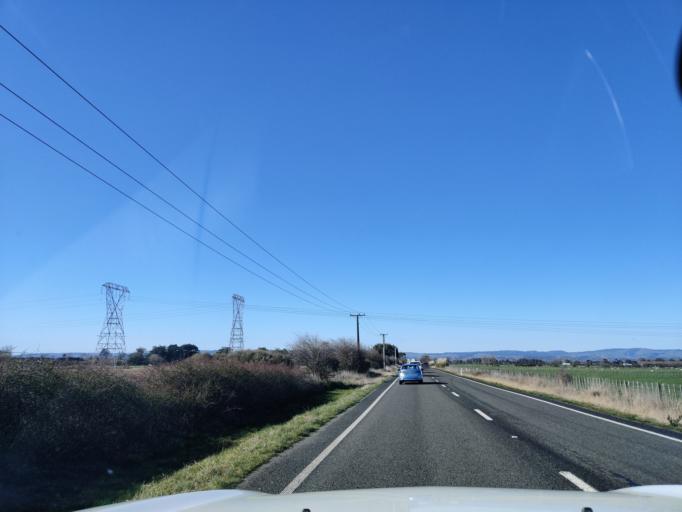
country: NZ
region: Manawatu-Wanganui
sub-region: Palmerston North City
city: Palmerston North
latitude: -40.2914
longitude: 175.5686
